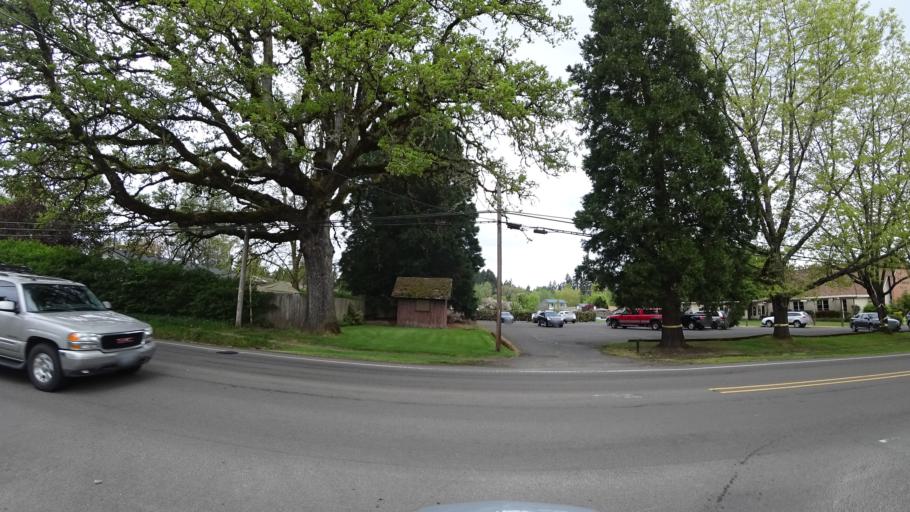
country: US
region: Oregon
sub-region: Washington County
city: Hillsboro
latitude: 45.5309
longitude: -122.9806
